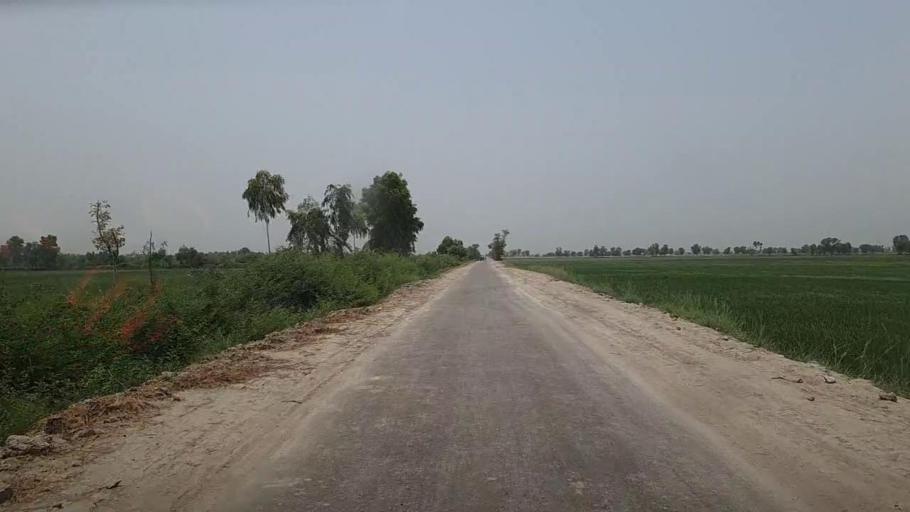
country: PK
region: Sindh
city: Sita Road
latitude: 27.0708
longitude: 67.9062
